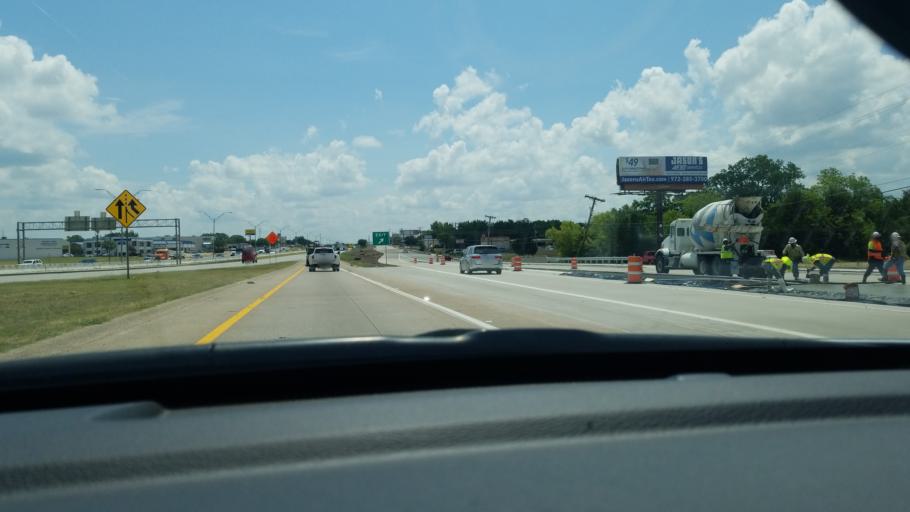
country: US
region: Texas
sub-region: Dallas County
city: Mesquite
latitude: 32.7924
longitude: -96.6204
